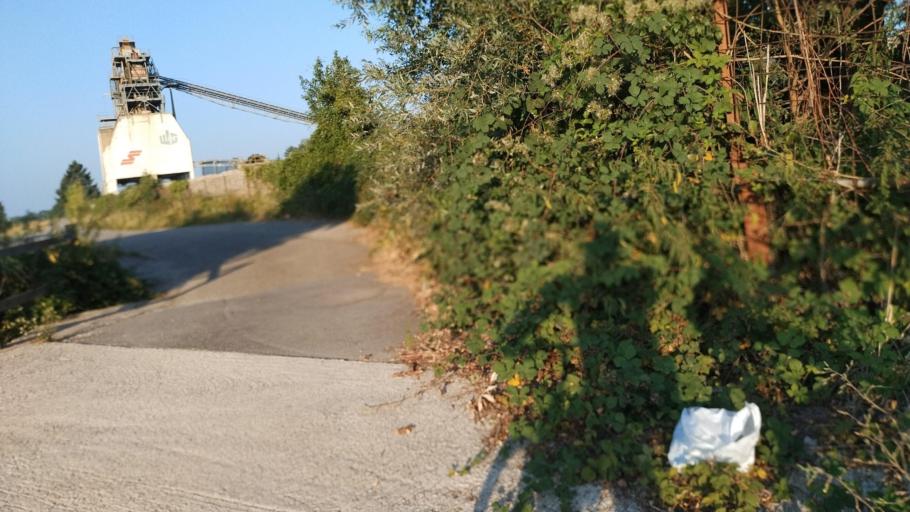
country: DE
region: Baden-Wuerttemberg
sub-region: Karlsruhe Region
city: Weingarten
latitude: 49.0725
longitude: 8.5315
